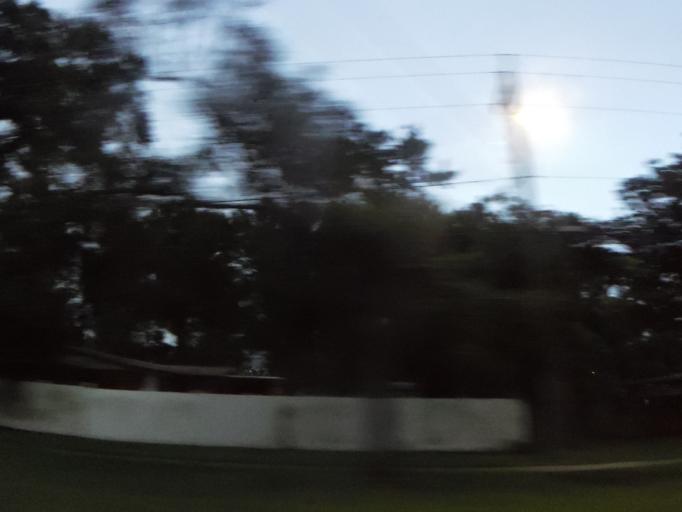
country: US
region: Florida
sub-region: Duval County
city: Jacksonville
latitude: 30.3671
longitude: -81.6079
